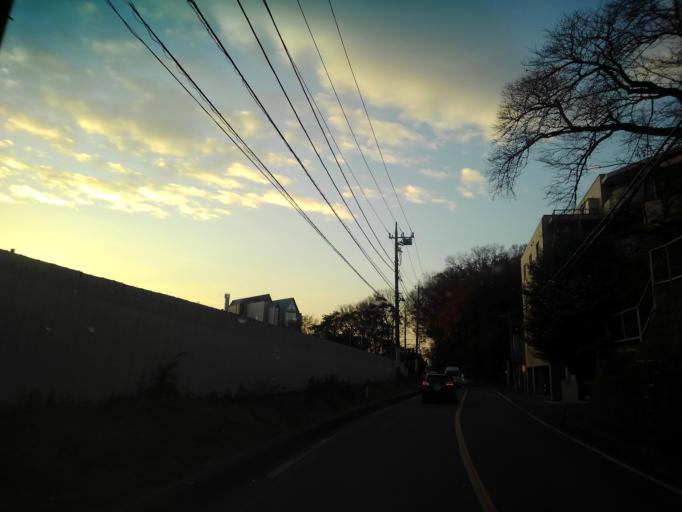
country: JP
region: Tokyo
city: Higashimurayama-shi
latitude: 35.7711
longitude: 139.4378
